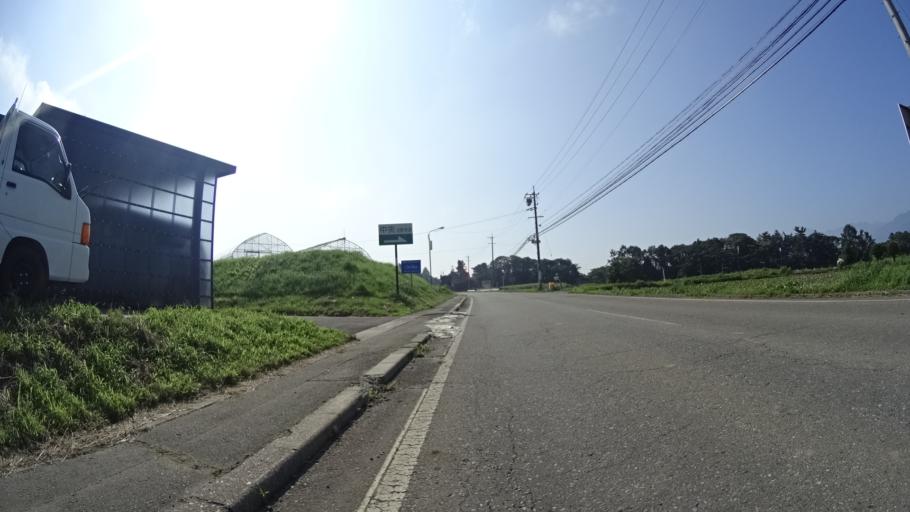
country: JP
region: Nagano
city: Chino
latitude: 35.9592
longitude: 138.2273
